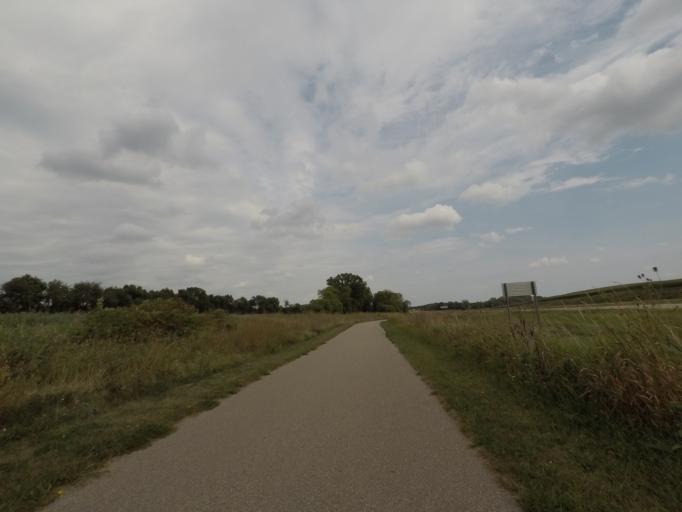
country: US
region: Wisconsin
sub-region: Jefferson County
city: Lake Koshkonong
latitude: 42.8481
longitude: -88.9165
